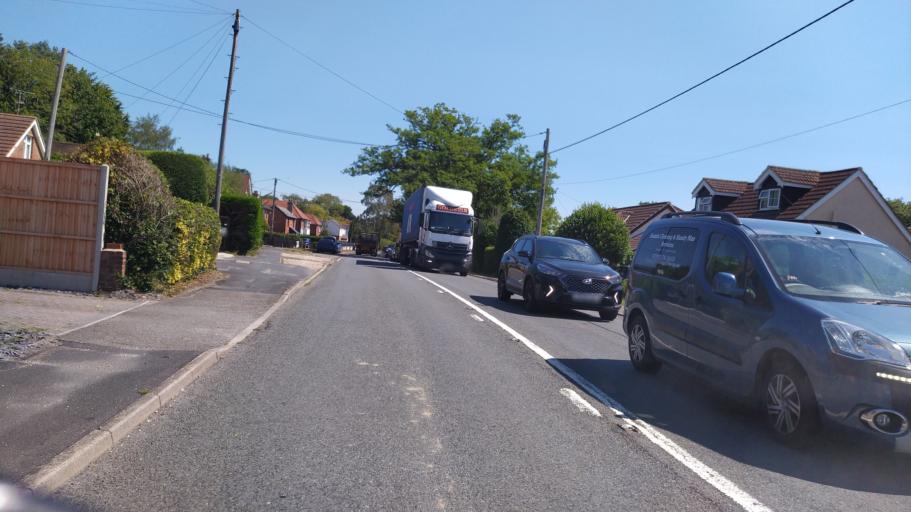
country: GB
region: England
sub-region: Hampshire
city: Cadnam
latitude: 50.9189
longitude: -1.5723
